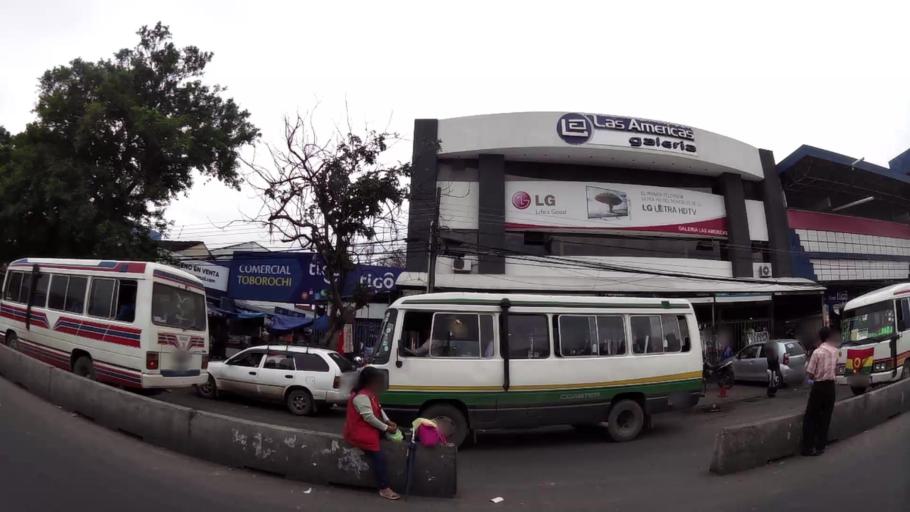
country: BO
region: Santa Cruz
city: Santa Cruz de la Sierra
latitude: -17.7943
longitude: -63.1882
